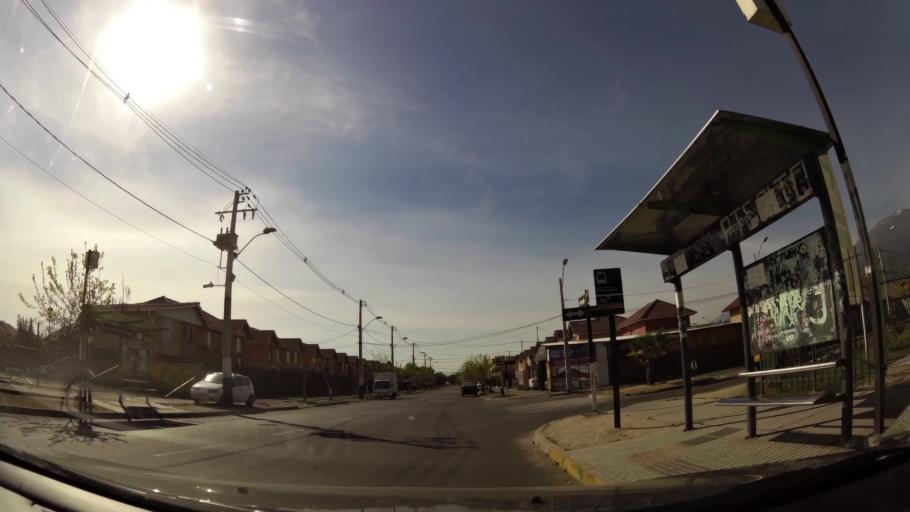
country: CL
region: Santiago Metropolitan
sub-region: Provincia de Cordillera
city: Puente Alto
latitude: -33.5886
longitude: -70.5566
